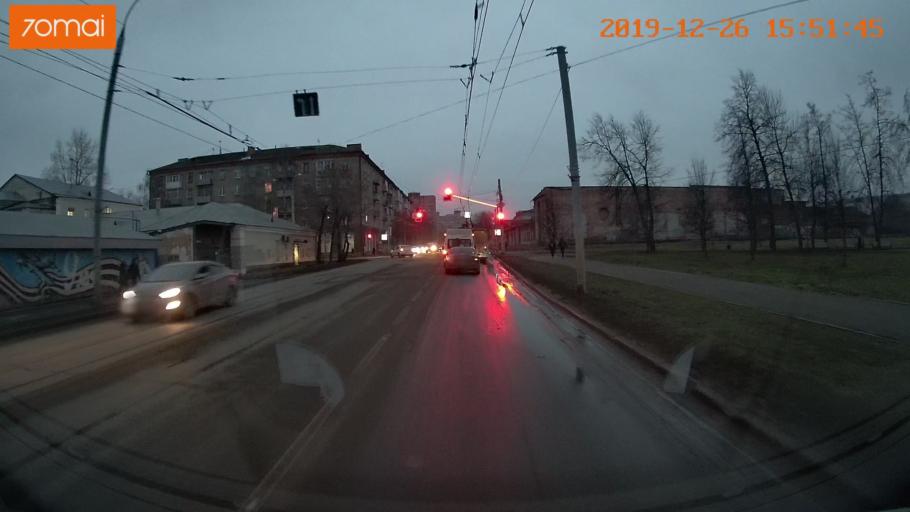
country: RU
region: Jaroslavl
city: Rybinsk
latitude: 58.0517
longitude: 38.8251
